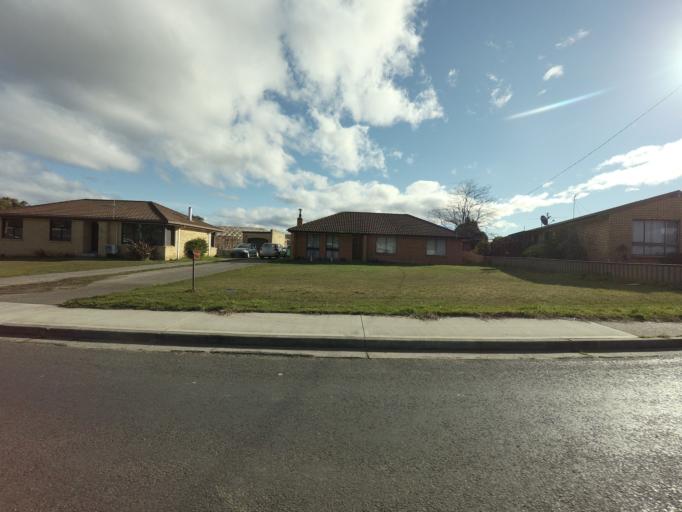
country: AU
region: Tasmania
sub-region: Derwent Valley
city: New Norfolk
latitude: -42.7675
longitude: 147.0457
